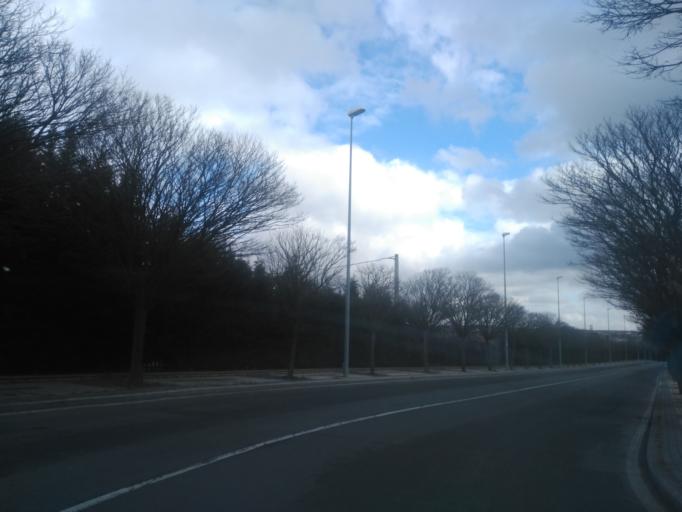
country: ES
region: Castille and Leon
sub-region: Provincia de Salamanca
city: Santa Marta de Tormes
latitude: 40.9745
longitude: -5.6356
